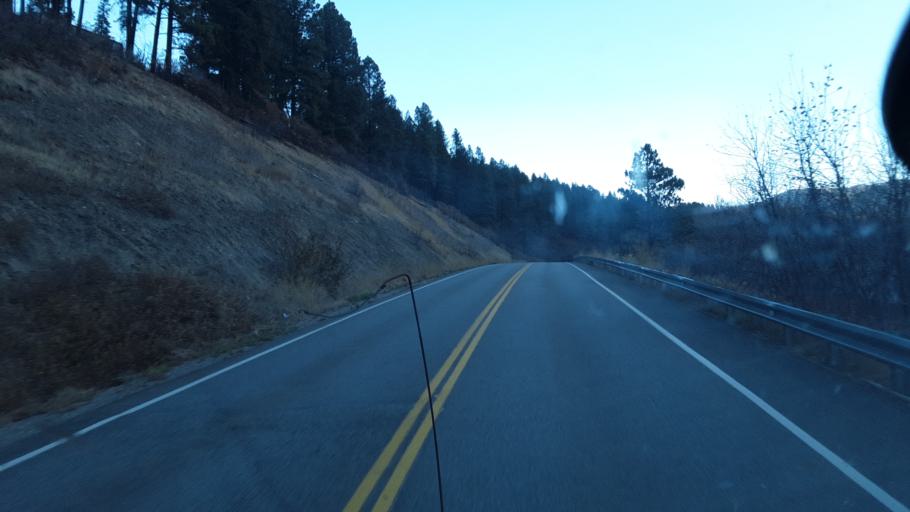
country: US
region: Colorado
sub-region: La Plata County
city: Bayfield
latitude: 37.3484
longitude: -107.6969
